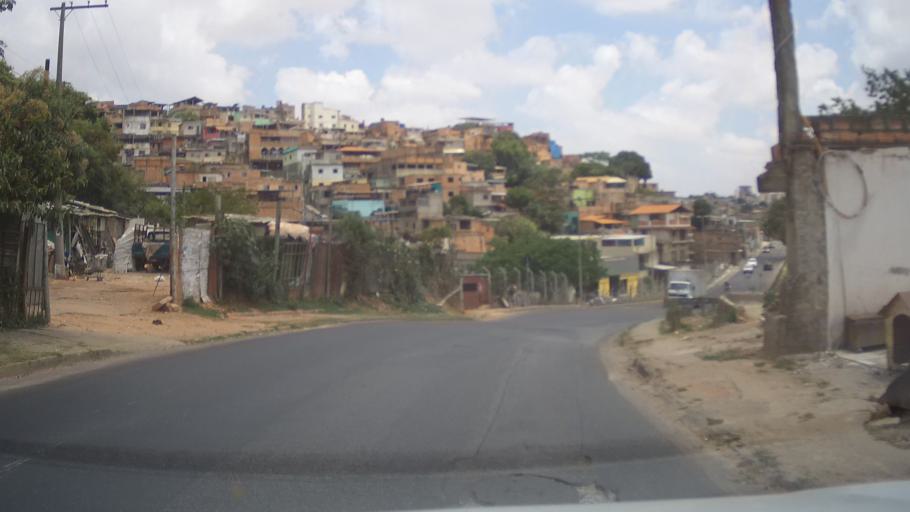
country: BR
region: Minas Gerais
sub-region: Belo Horizonte
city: Belo Horizonte
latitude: -19.9065
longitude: -43.8874
